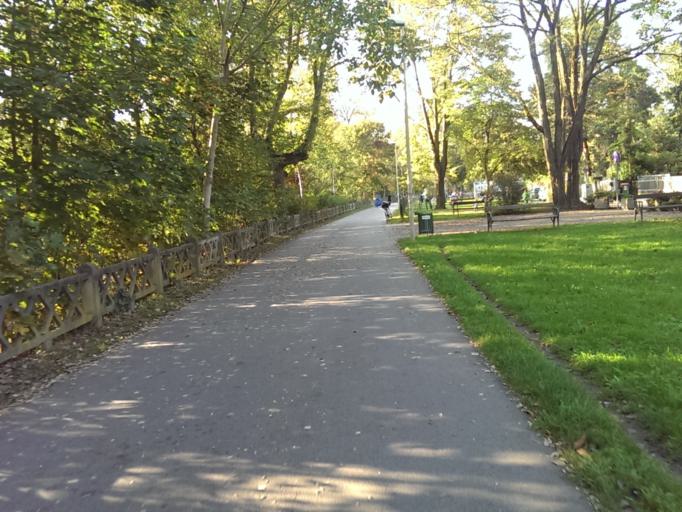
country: AT
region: Styria
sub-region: Graz Stadt
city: Graz
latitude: 47.0839
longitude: 15.4270
